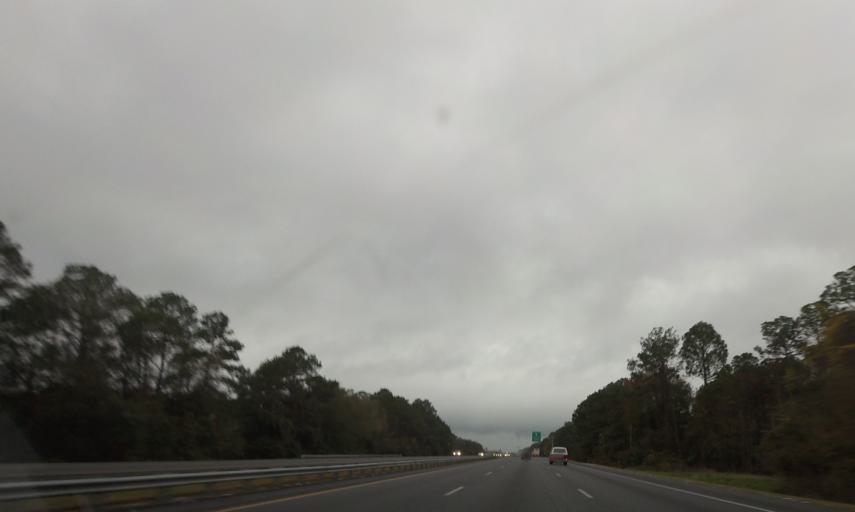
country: US
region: Georgia
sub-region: Lowndes County
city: Valdosta
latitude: 30.7344
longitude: -83.2638
